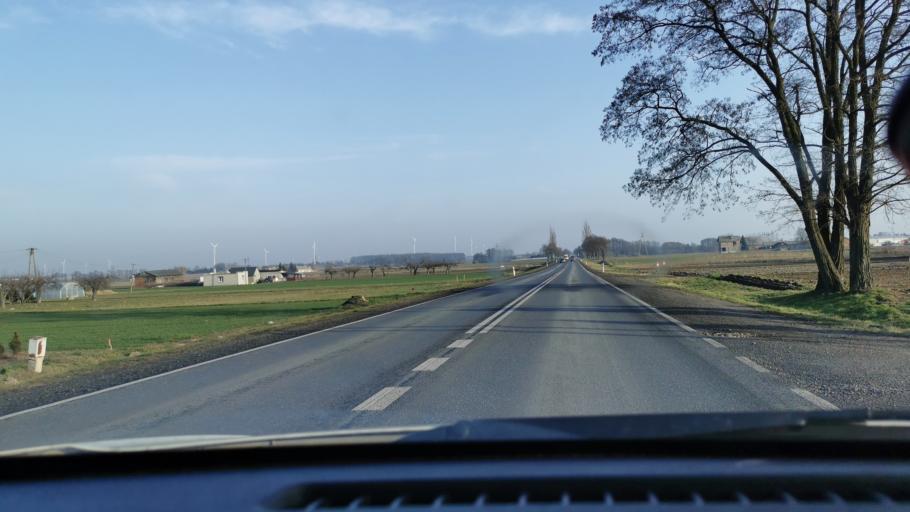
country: PL
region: Lodz Voivodeship
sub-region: Powiat sieradzki
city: Blaszki
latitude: 51.6437
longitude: 18.4835
